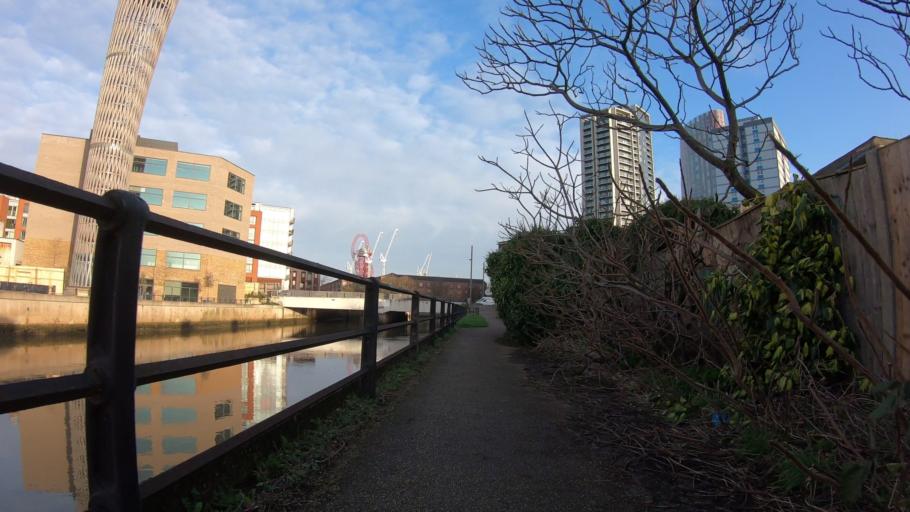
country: GB
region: England
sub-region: Greater London
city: Poplar
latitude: 51.5296
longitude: -0.0068
